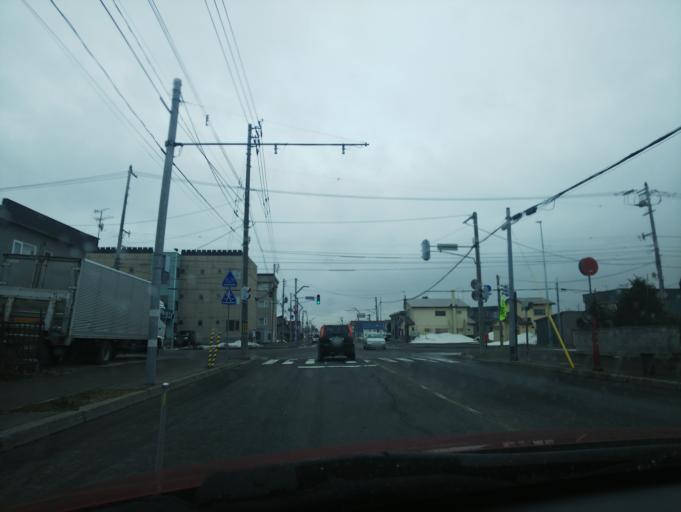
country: JP
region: Hokkaido
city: Nayoro
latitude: 44.3467
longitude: 142.4503
